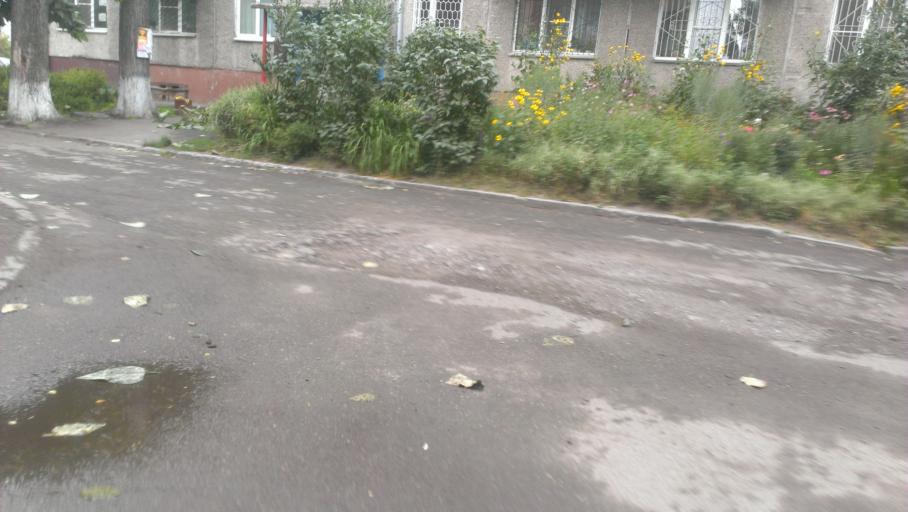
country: RU
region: Altai Krai
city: Novosilikatnyy
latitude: 53.3741
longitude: 83.6699
